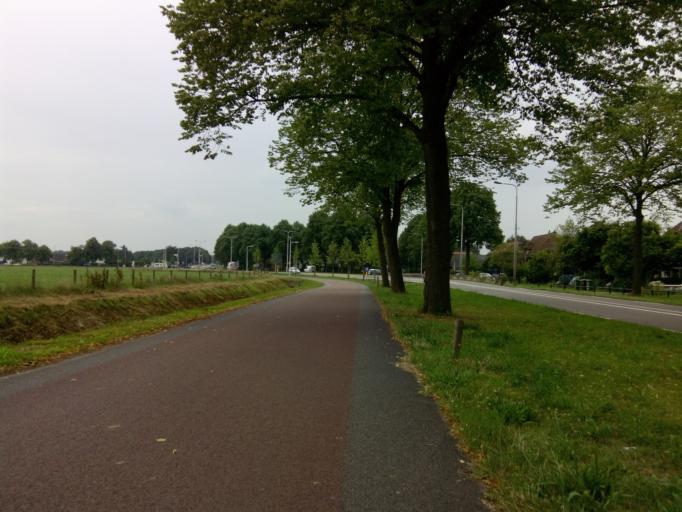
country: NL
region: Utrecht
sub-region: Gemeente Leusden
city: Leusden
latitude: 52.1757
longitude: 5.4367
